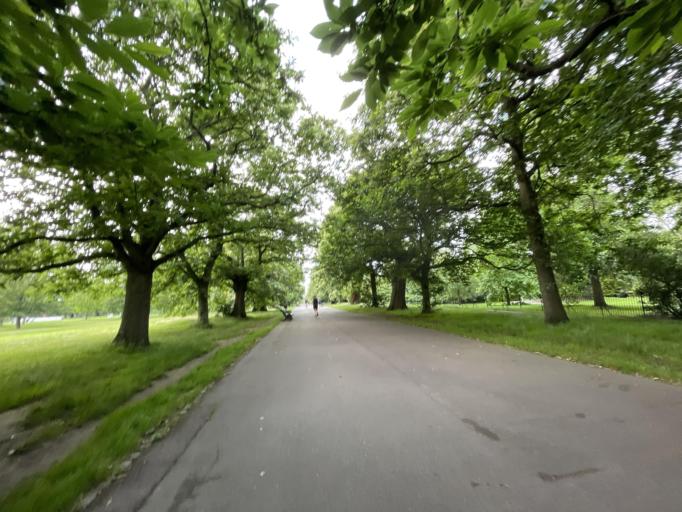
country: GB
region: England
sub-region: Greater London
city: Blackheath
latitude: 51.4756
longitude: 0.0037
